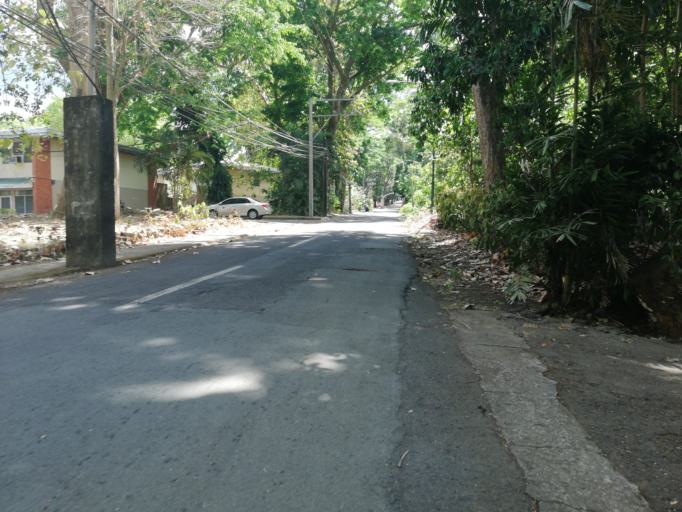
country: PH
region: Calabarzon
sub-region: Province of Laguna
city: Los Banos
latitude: 14.1590
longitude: 121.2374
